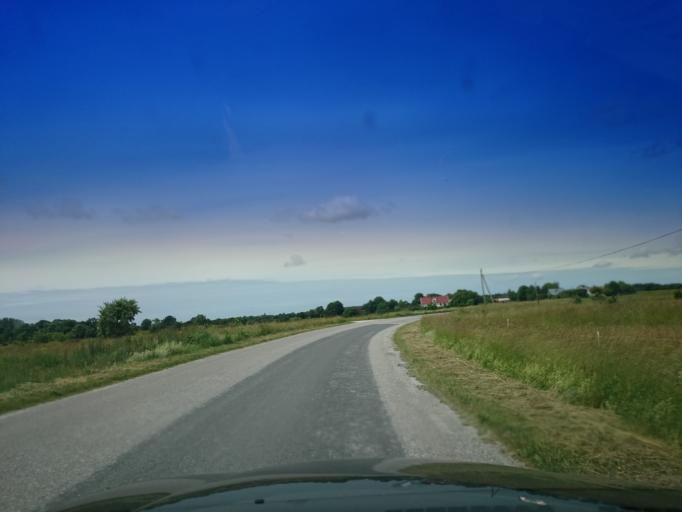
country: SE
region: Gotland
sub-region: Gotland
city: Hemse
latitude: 57.2478
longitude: 18.5527
